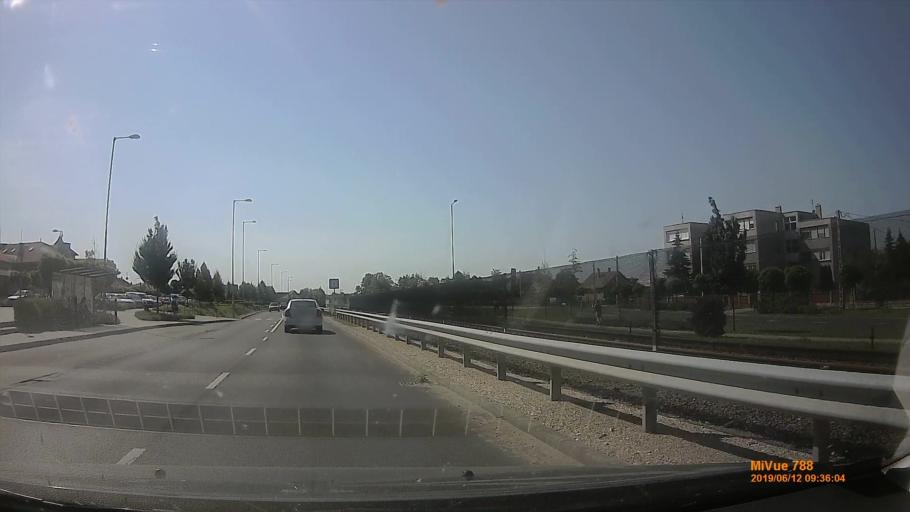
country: HU
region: Pest
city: Gyal
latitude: 47.3815
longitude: 19.2143
